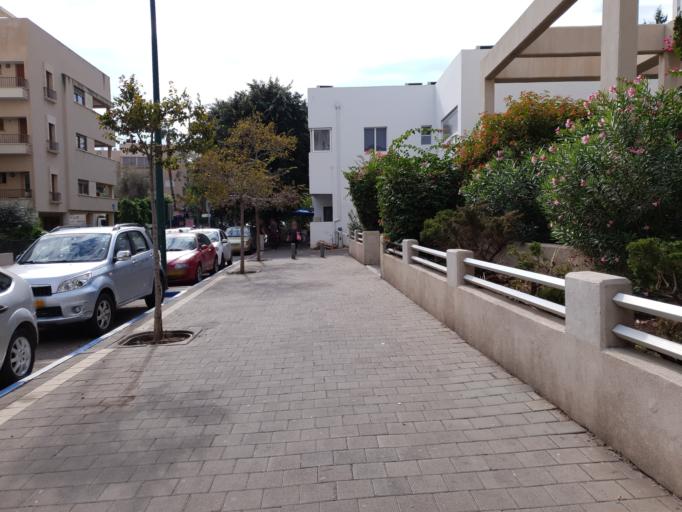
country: IL
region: Tel Aviv
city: Tel Aviv
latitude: 32.0841
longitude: 34.7766
